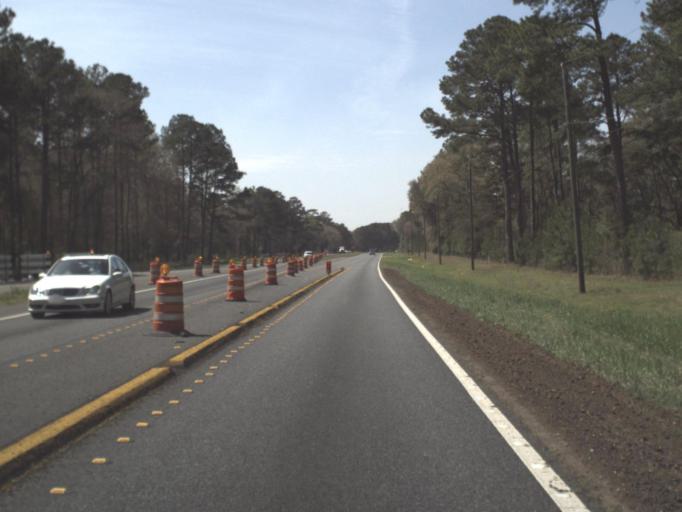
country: US
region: Florida
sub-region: Gadsden County
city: Quincy
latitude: 30.5540
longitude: -84.5177
